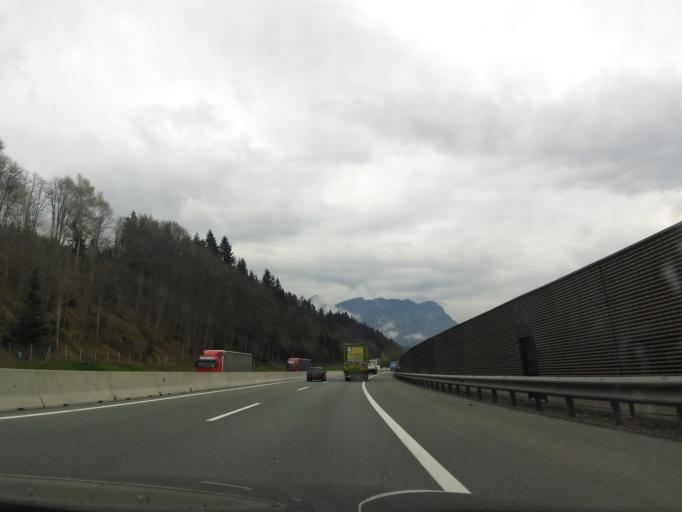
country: AT
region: Tyrol
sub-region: Politischer Bezirk Kufstein
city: Angath
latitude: 47.5038
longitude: 12.0580
